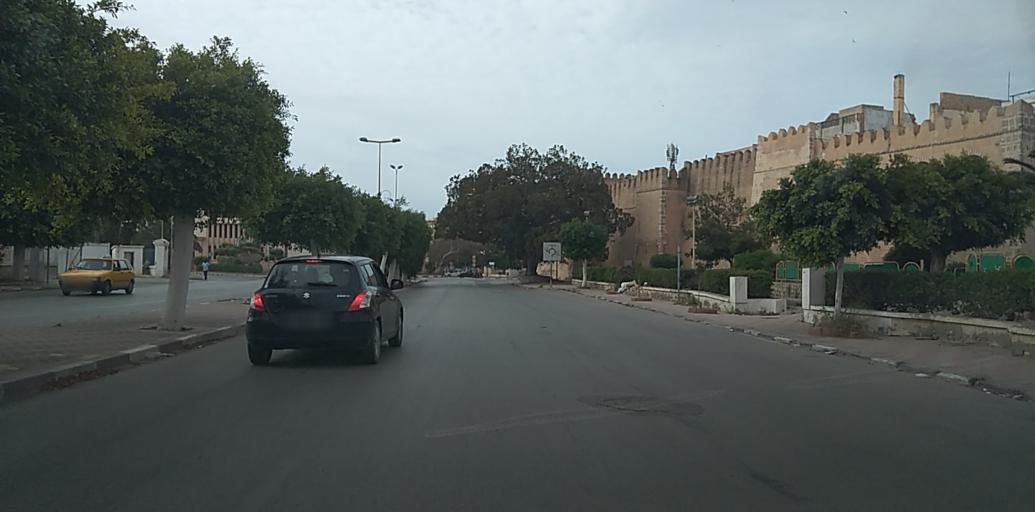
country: TN
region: Safaqis
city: Sfax
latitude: 34.7364
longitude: 10.7645
